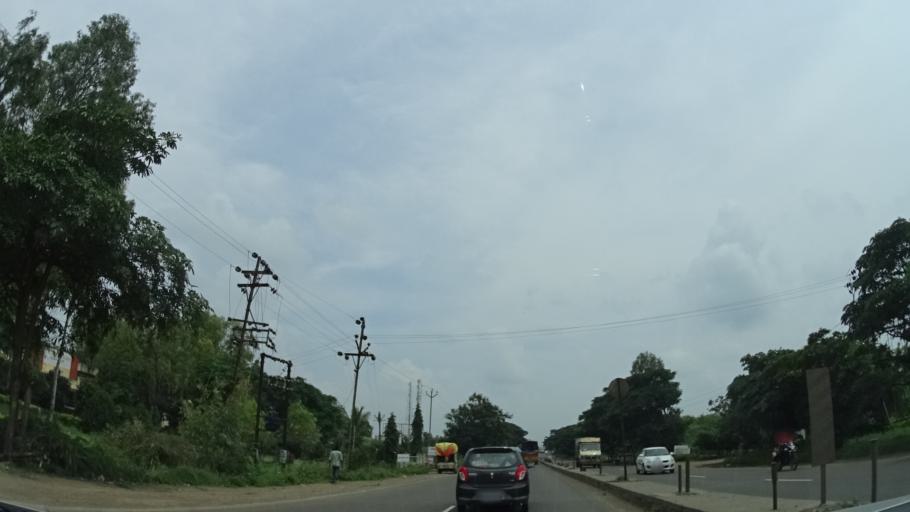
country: IN
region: Maharashtra
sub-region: Pune Division
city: Koregaon
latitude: 18.7225
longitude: 74.1924
